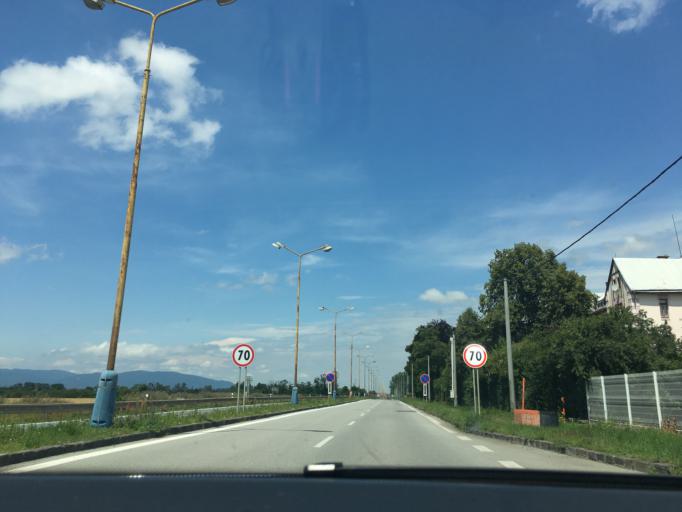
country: SK
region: Kosicky
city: Trebisov
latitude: 48.6448
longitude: 21.7155
